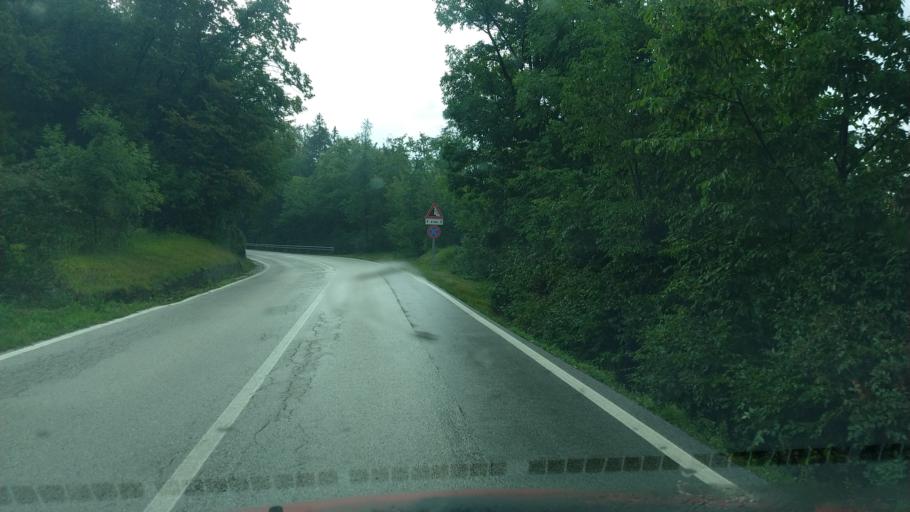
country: IT
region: Veneto
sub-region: Provincia di Vicenza
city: Tonezza del Cimone
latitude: 45.8529
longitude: 11.3554
